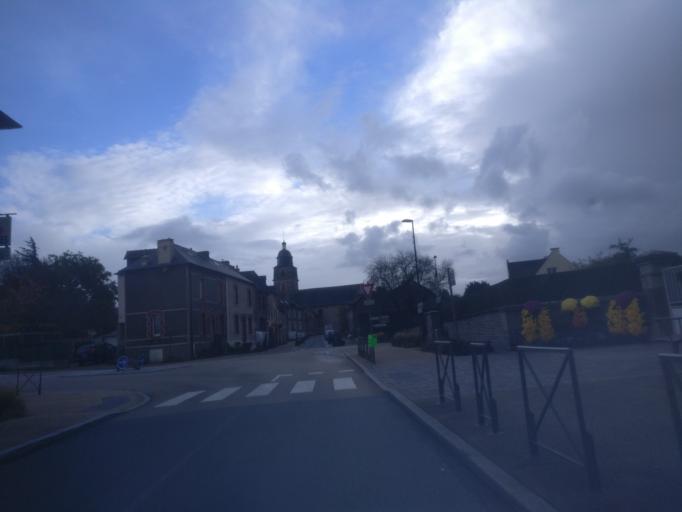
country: FR
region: Brittany
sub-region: Departement d'Ille-et-Vilaine
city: Breal-sous-Montfort
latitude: 48.0500
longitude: -1.8684
